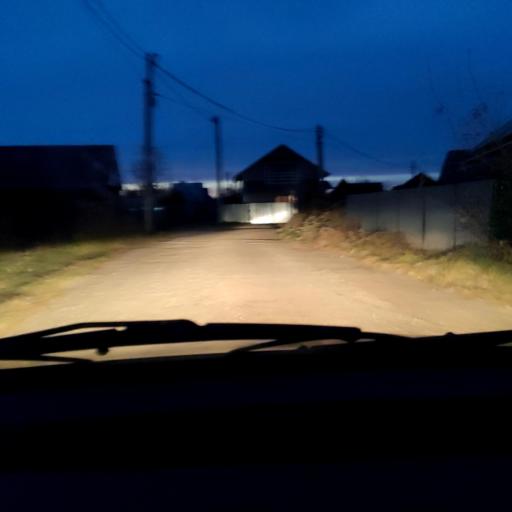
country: RU
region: Bashkortostan
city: Mikhaylovka
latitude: 54.7908
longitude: 55.8318
